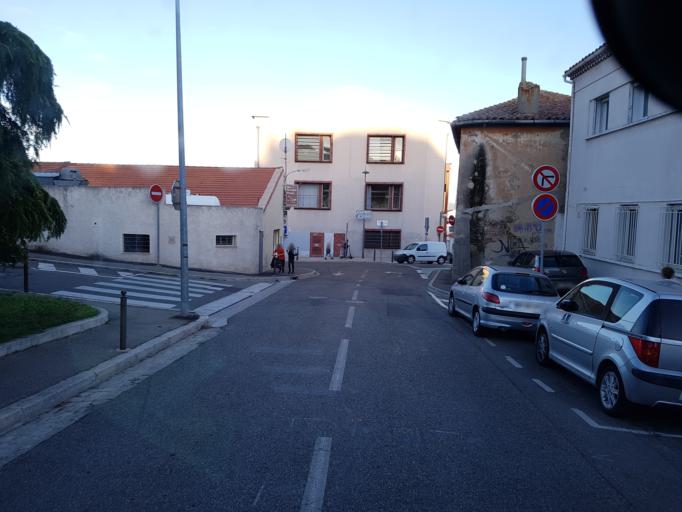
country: FR
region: Provence-Alpes-Cote d'Azur
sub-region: Departement des Bouches-du-Rhone
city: La Ciotat
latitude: 43.1711
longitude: 5.6024
